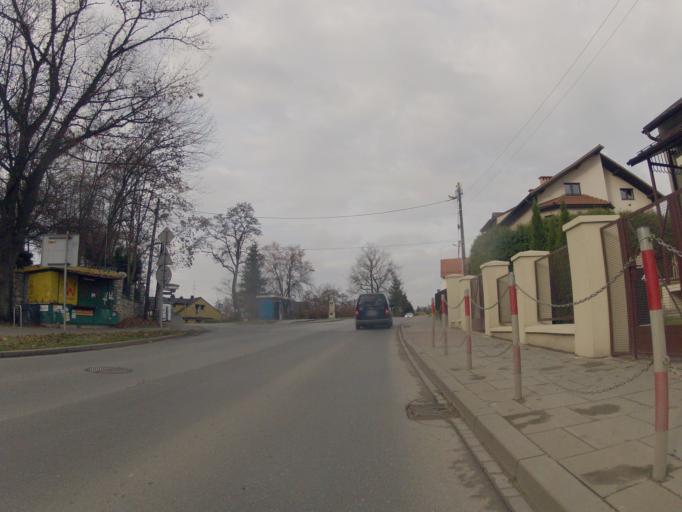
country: PL
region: Lesser Poland Voivodeship
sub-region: Powiat krakowski
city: Rzaska
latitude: 50.0841
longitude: 19.8459
